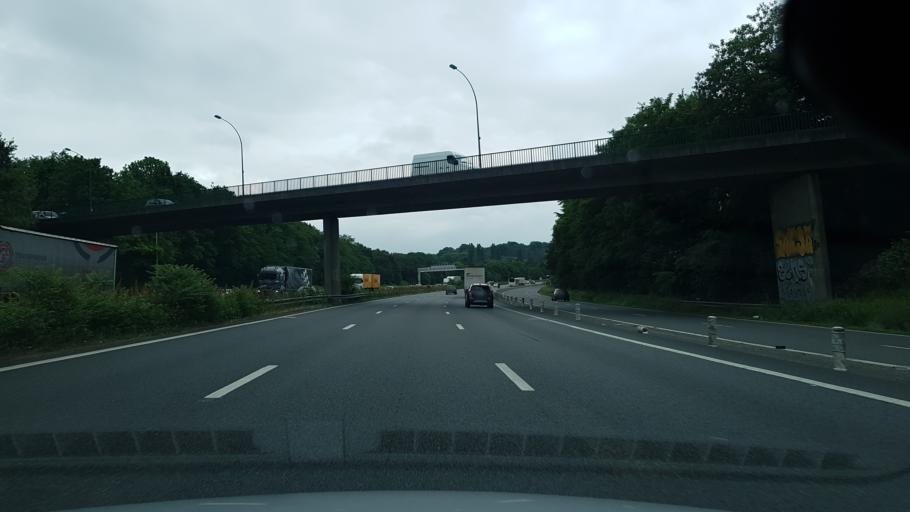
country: FR
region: Ile-de-France
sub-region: Departement de l'Essonne
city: Villebon-sur-Yvette
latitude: 48.7008
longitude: 2.2466
